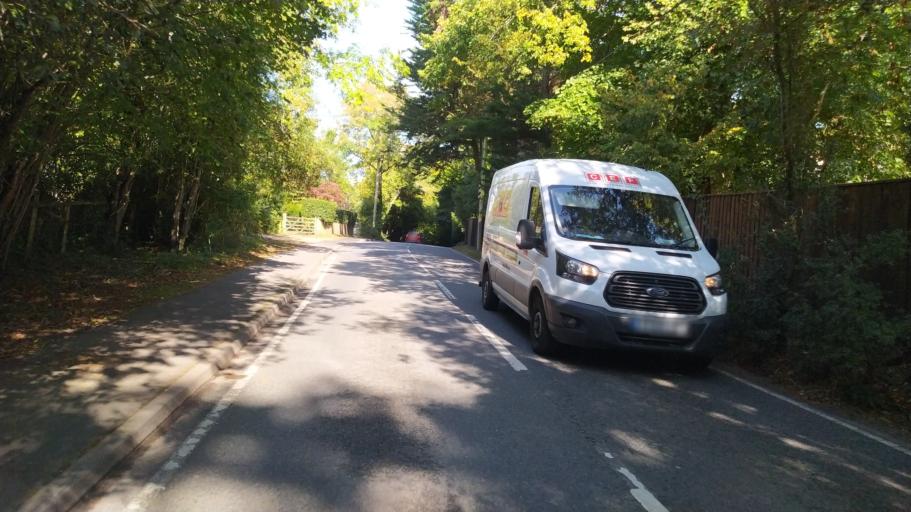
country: GB
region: England
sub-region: Hampshire
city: Bransgore
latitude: 50.8342
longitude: -1.7115
